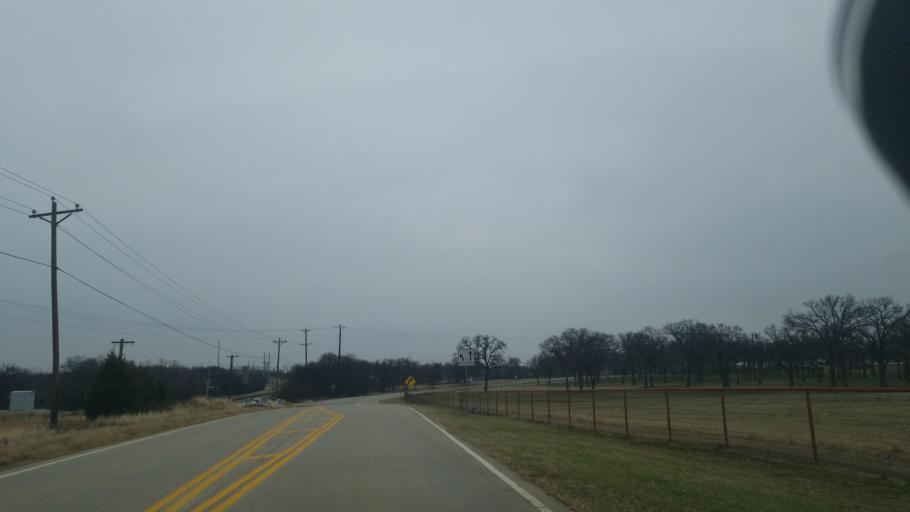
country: US
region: Texas
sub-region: Denton County
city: Copper Canyon
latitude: 33.1160
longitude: -97.1085
